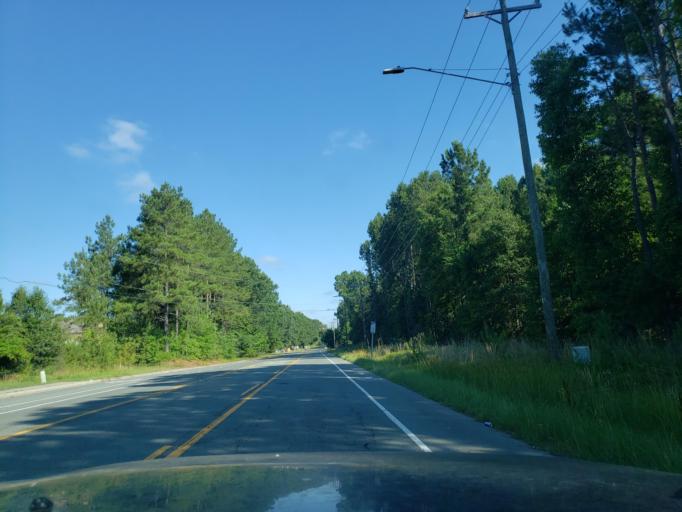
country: US
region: North Carolina
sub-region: Durham County
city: Durham
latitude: 35.9349
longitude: -78.8917
